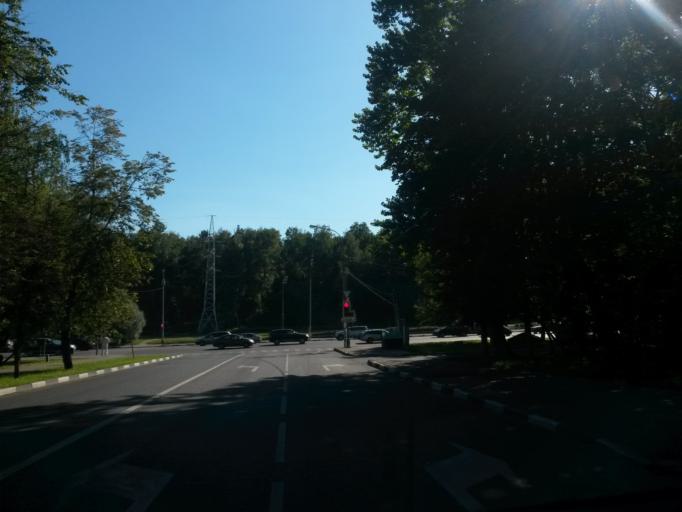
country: RU
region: Moscow
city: Zyuzino
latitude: 55.6472
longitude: 37.5772
